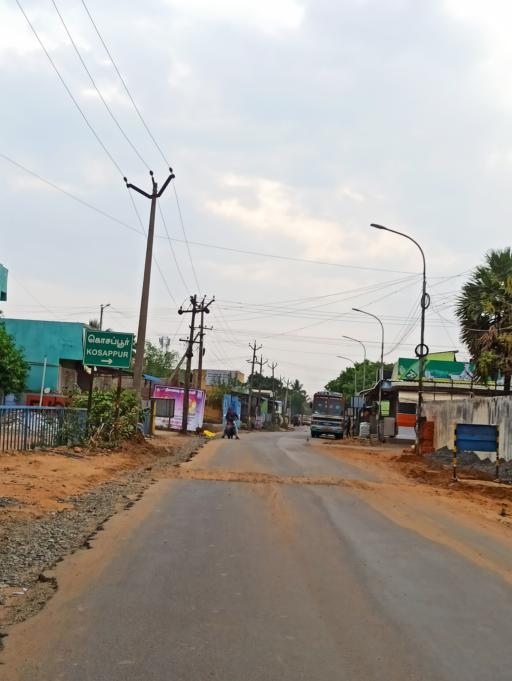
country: IN
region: Tamil Nadu
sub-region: Thiruvallur
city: Chinnasekkadu
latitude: 13.1681
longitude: 80.2366
